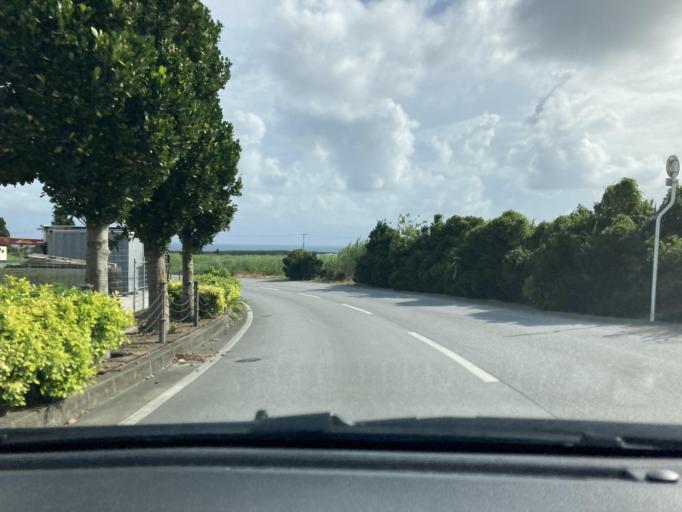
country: JP
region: Okinawa
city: Itoman
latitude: 26.0938
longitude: 127.6932
